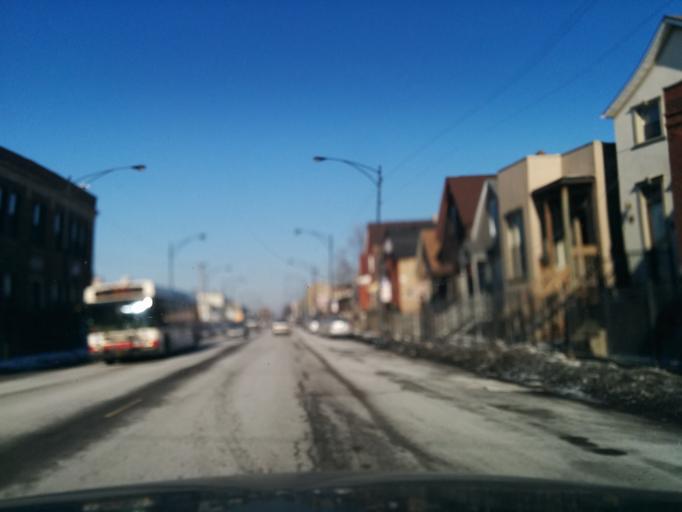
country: US
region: Illinois
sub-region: Cook County
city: Chicago
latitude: 41.8928
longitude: -87.6928
